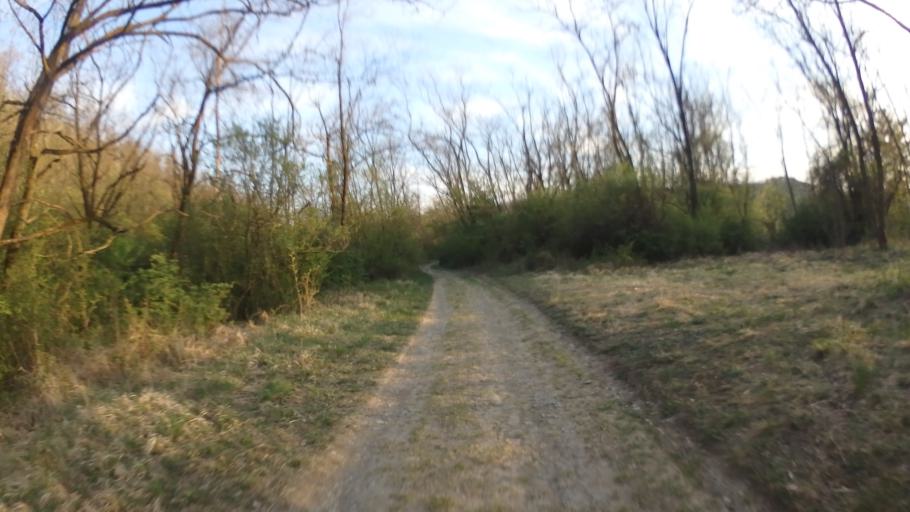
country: CZ
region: South Moravian
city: Zelesice
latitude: 49.1312
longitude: 16.5567
